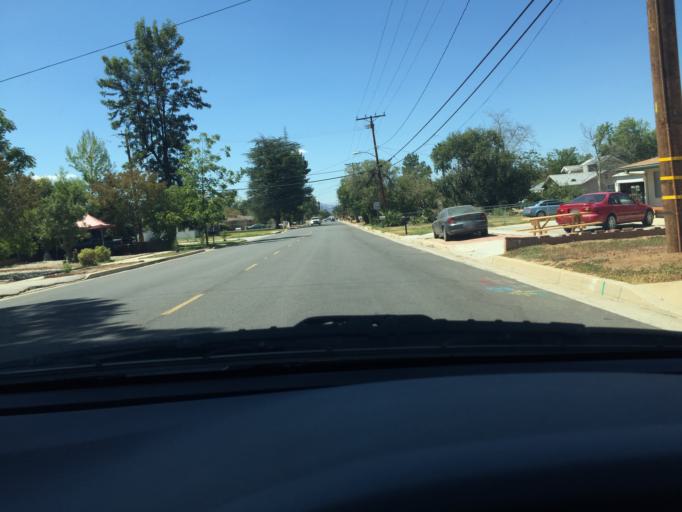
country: US
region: California
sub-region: Riverside County
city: Calimesa
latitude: 33.9995
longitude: -117.0434
